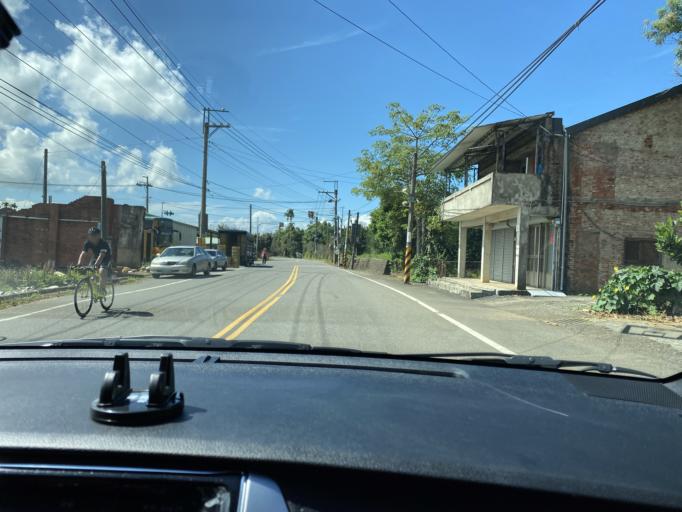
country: TW
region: Taiwan
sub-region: Nantou
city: Nantou
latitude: 23.8775
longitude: 120.6327
